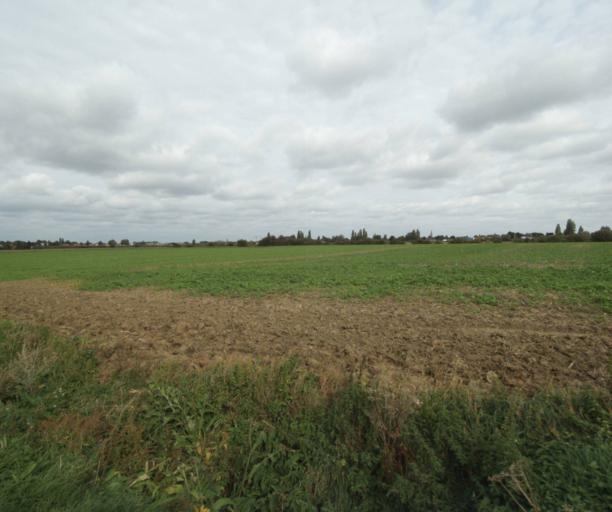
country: FR
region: Nord-Pas-de-Calais
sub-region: Departement du Nord
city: Erquinghem-Lys
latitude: 50.6700
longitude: 2.8611
